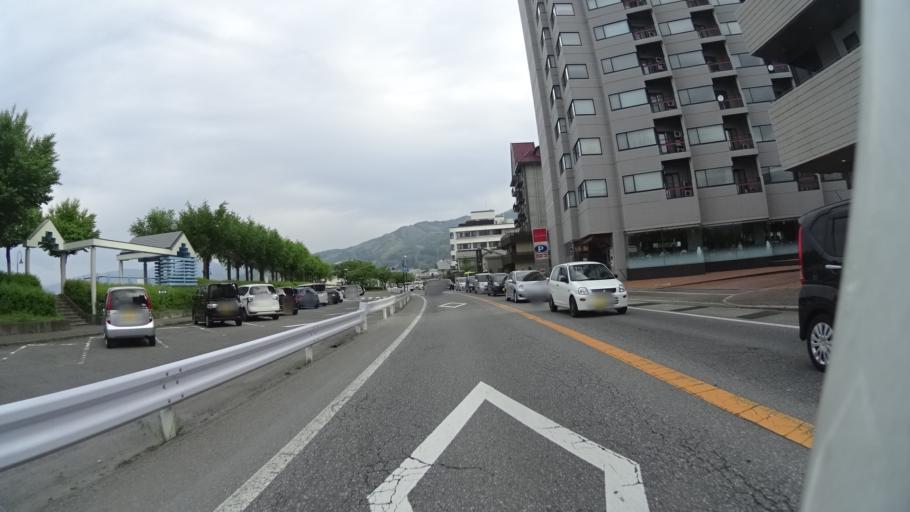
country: JP
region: Nagano
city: Suwa
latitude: 36.0513
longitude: 138.1129
